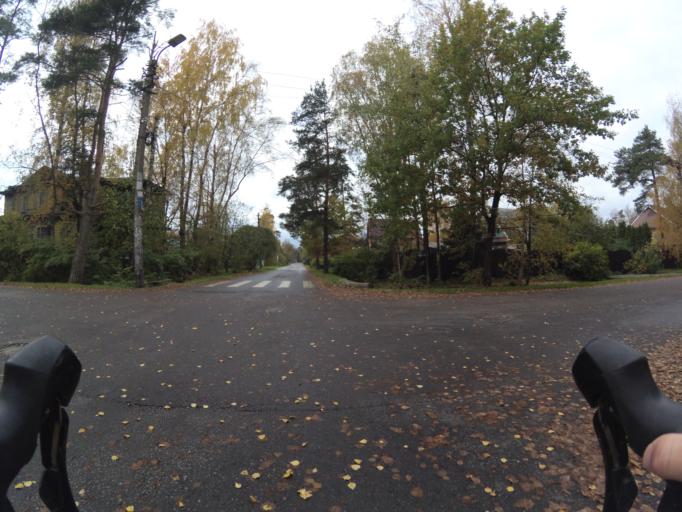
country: RU
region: St.-Petersburg
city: Lakhtinskiy
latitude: 60.0013
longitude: 30.1380
